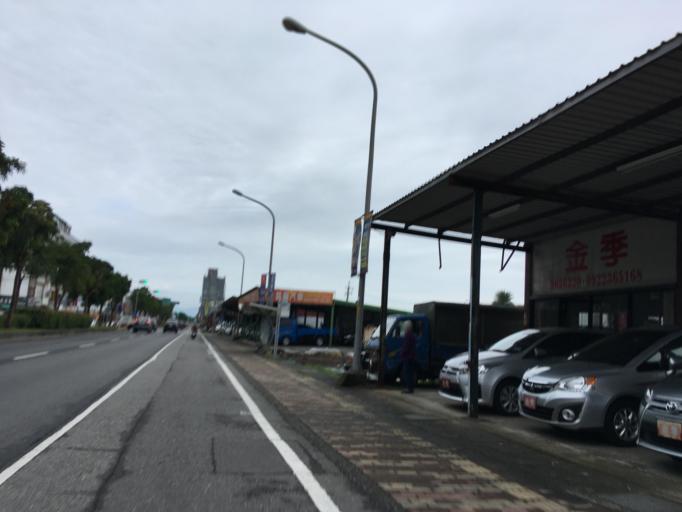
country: TW
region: Taiwan
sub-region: Yilan
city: Yilan
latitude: 24.7030
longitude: 121.7703
